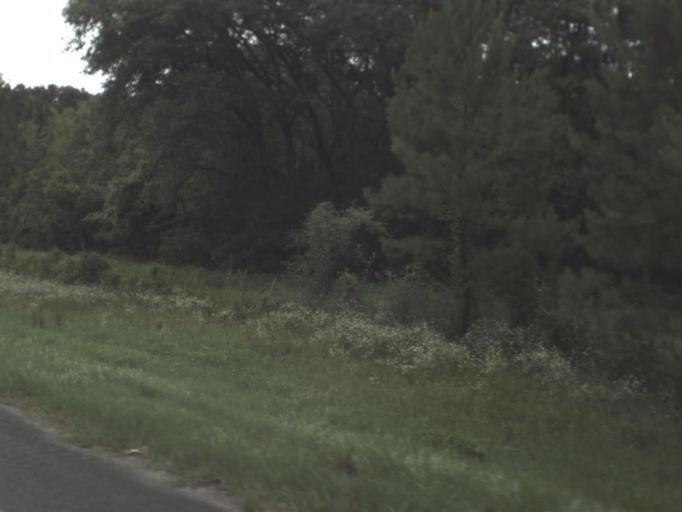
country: US
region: Florida
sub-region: Alachua County
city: Archer
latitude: 29.4894
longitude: -82.4927
